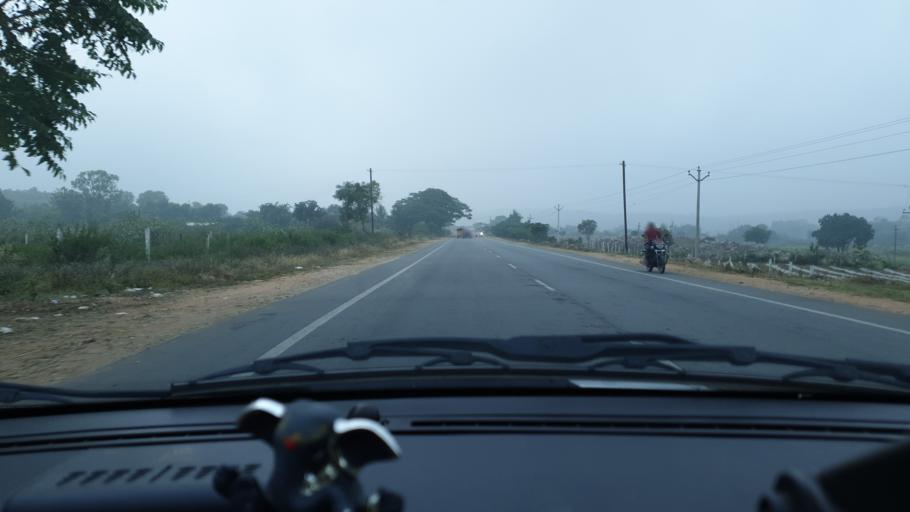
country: IN
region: Telangana
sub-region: Mahbubnagar
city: Farrukhnagar
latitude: 16.9614
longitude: 78.5118
